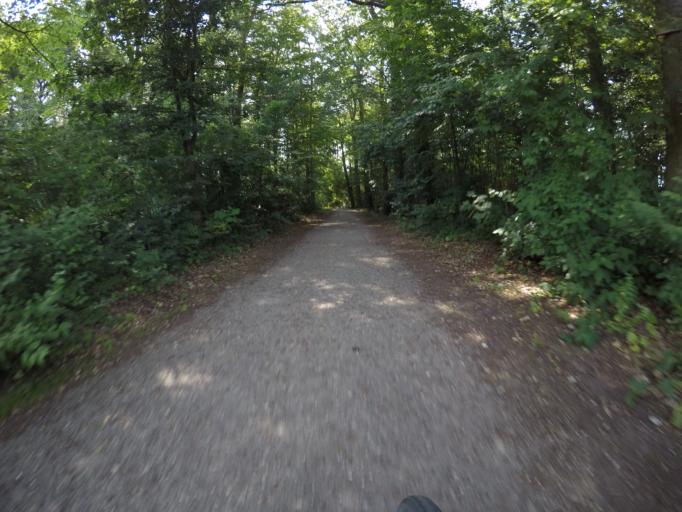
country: DE
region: Baden-Wuerttemberg
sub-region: Regierungsbezirk Stuttgart
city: Steinenbronn
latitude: 48.7005
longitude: 9.1297
